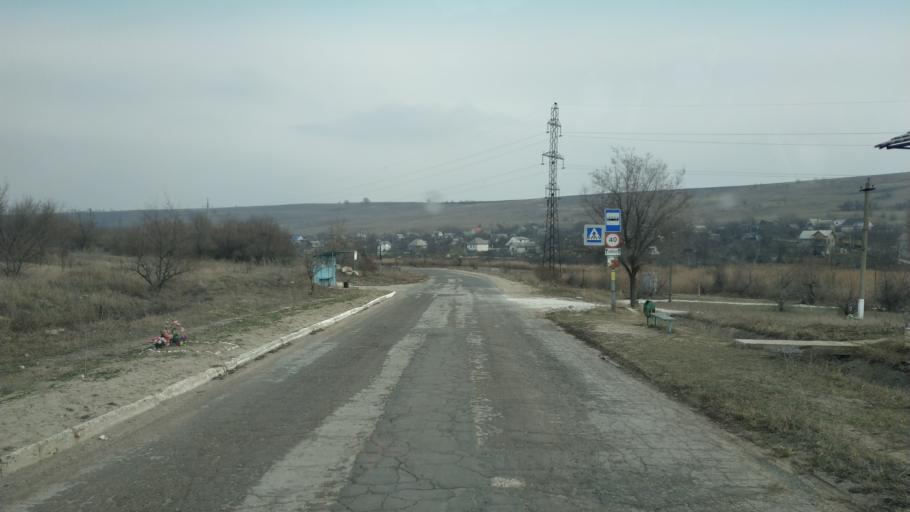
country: MD
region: Chisinau
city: Singera
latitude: 46.8929
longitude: 29.0135
